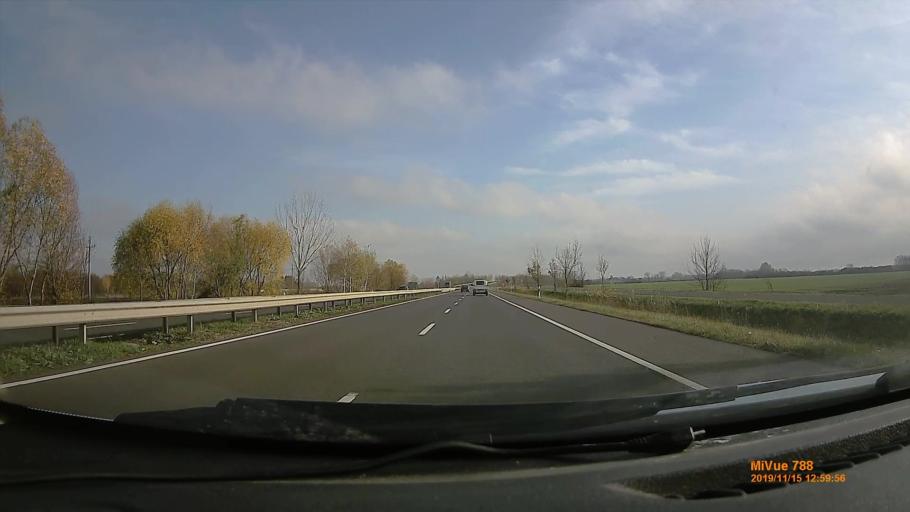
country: HU
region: Bekes
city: Gyula
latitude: 46.6639
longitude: 21.1989
